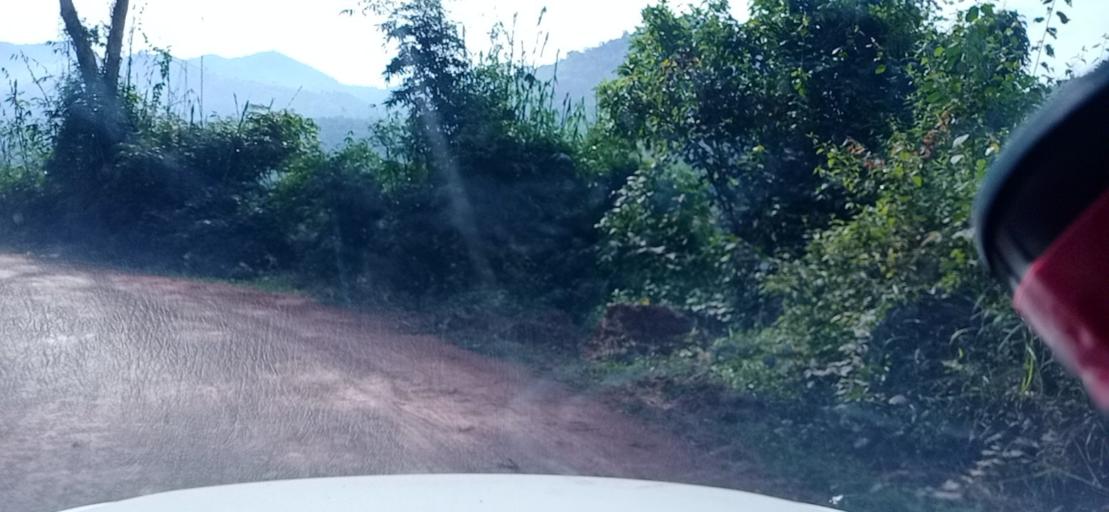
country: TH
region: Changwat Bueng Kan
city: Pak Khat
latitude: 18.6704
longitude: 103.1946
